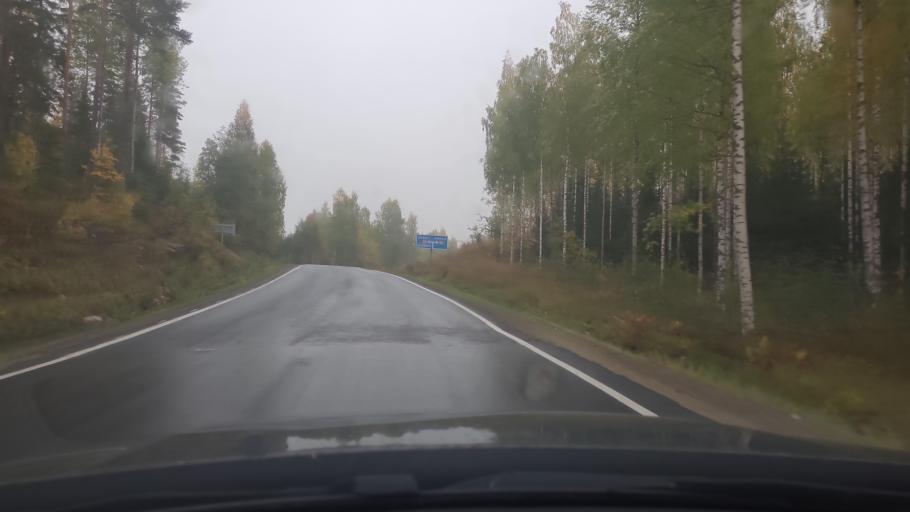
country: FI
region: Northern Savo
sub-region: Varkaus
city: Kangaslampi
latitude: 62.4546
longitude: 28.2766
